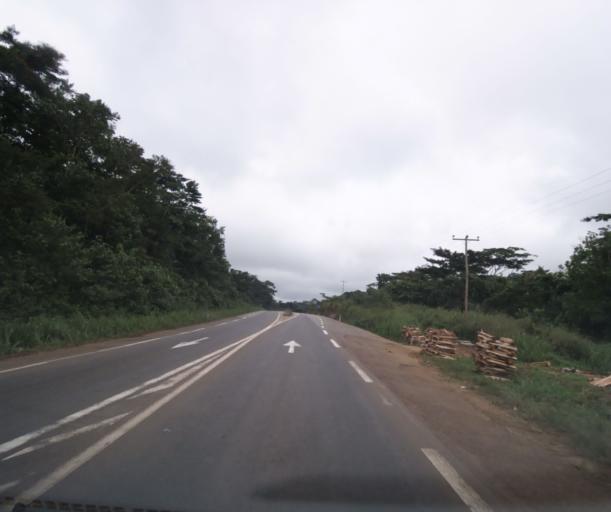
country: CM
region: Centre
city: Mbankomo
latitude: 3.7957
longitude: 11.3731
